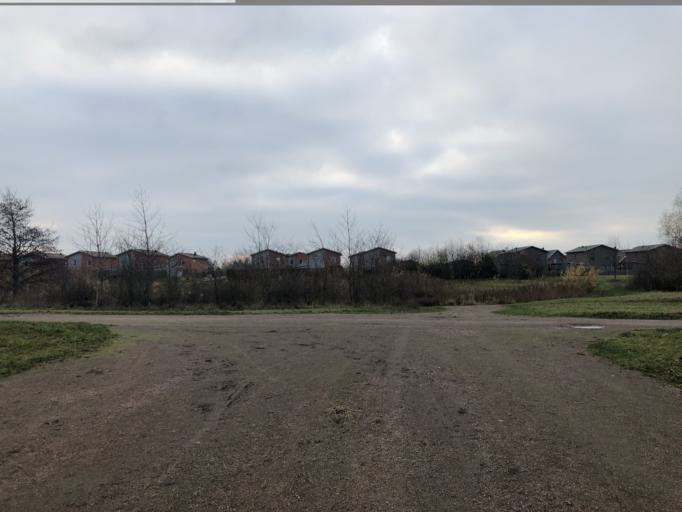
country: SE
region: Skane
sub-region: Malmo
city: Tygelsjo
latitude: 55.5202
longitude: 12.9900
